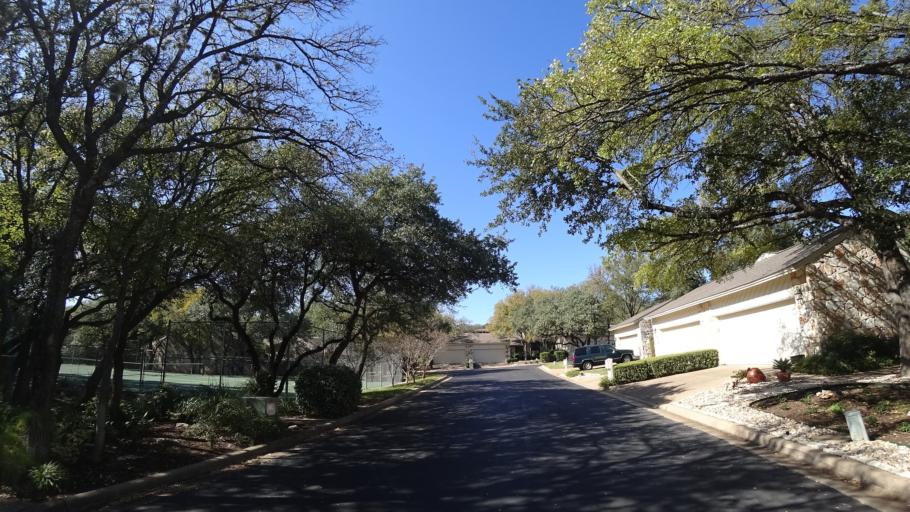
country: US
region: Texas
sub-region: Williamson County
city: Jollyville
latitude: 30.3737
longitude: -97.7442
